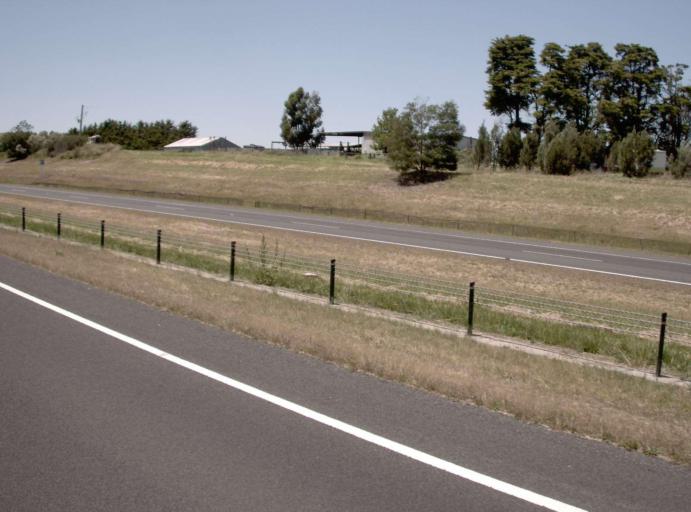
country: AU
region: Victoria
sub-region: Cardinia
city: Pakenham Upper
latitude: -38.0736
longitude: 145.5459
